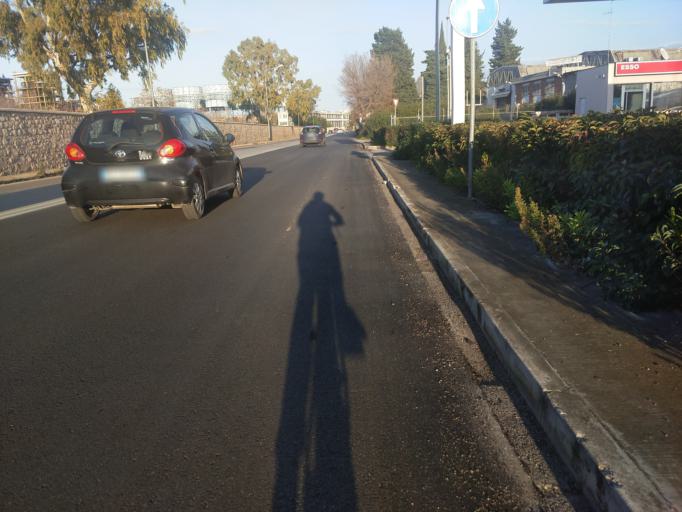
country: IT
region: Apulia
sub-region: Provincia di Bari
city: Bari
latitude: 41.1144
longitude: 16.8335
